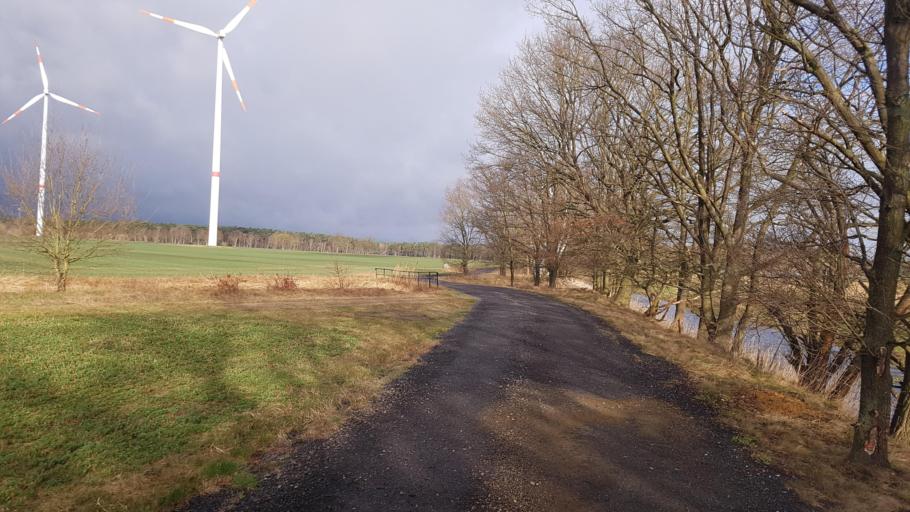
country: DE
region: Brandenburg
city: Bronkow
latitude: 51.6482
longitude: 13.8846
